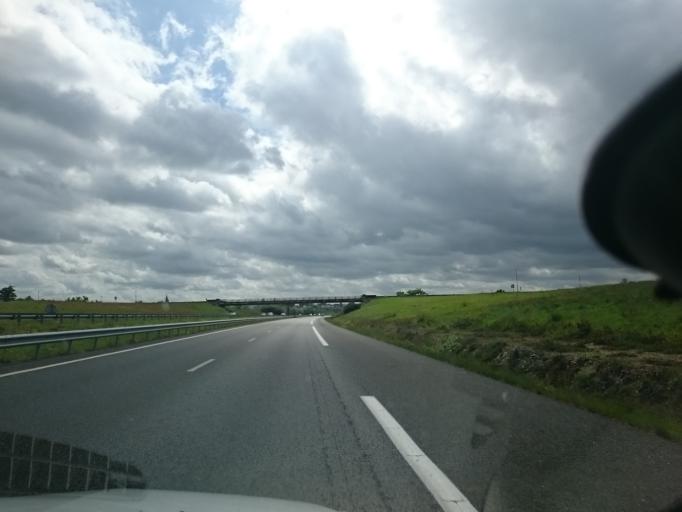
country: FR
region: Brittany
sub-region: Departement d'Ille-et-Vilaine
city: Liffre
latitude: 48.2229
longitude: -1.4973
